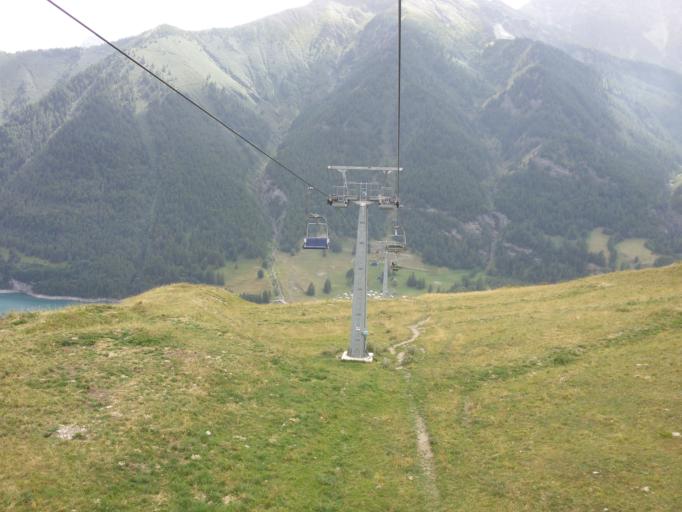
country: IT
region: Piedmont
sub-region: Provincia di Cuneo
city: Pontechianale
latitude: 44.6294
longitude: 7.0347
